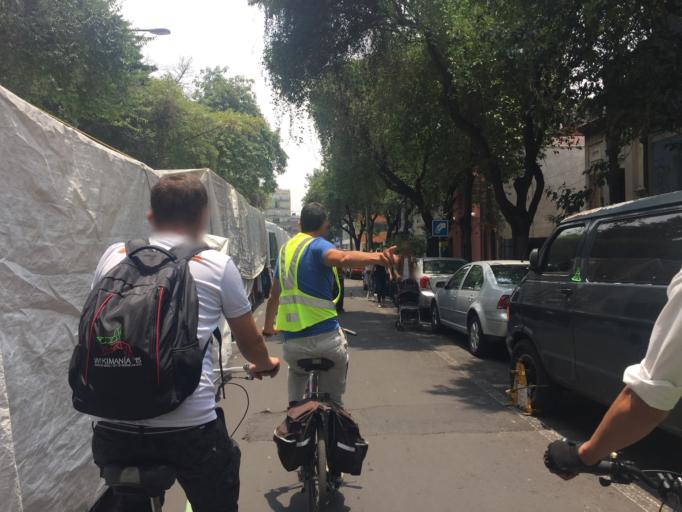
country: MX
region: Mexico City
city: Benito Juarez
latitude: 19.4208
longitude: -99.1553
